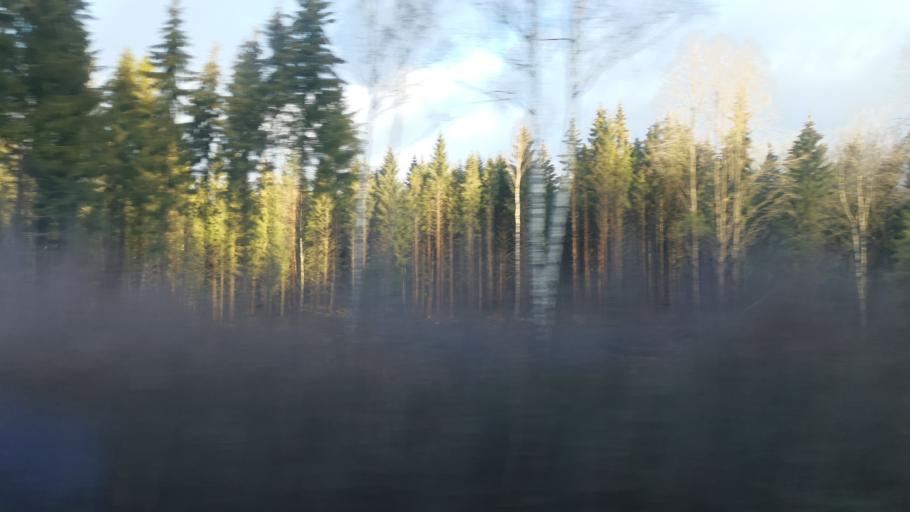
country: SE
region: Soedermanland
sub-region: Vingakers Kommun
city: Vingaker
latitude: 59.0523
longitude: 15.6938
